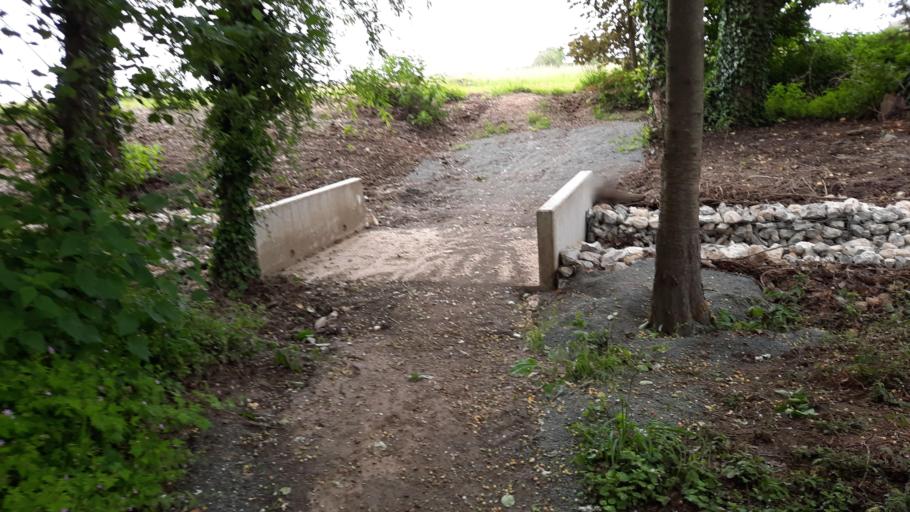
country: BE
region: Flanders
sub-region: Provincie Limburg
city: Hoeselt
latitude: 50.8494
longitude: 5.4532
